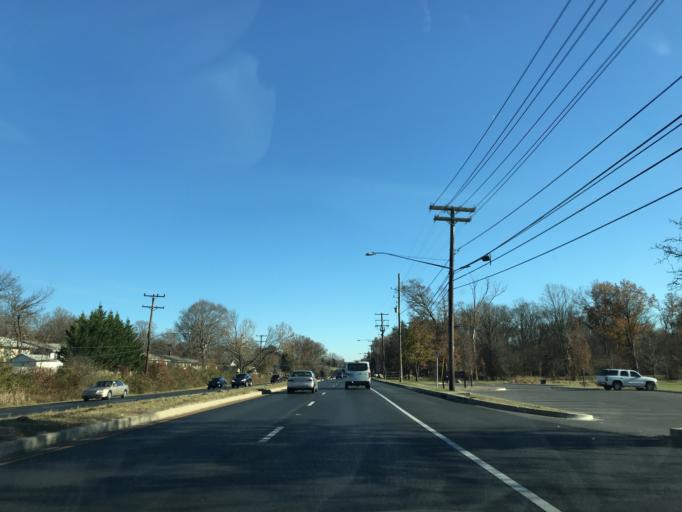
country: US
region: Maryland
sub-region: Montgomery County
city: North Bethesda
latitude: 39.0682
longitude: -77.1033
